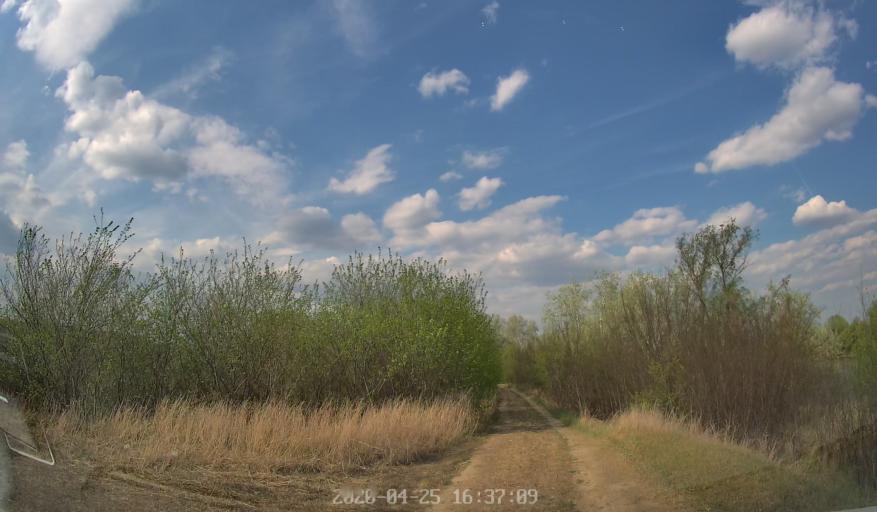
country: MD
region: Chisinau
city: Vadul lui Voda
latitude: 47.1122
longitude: 29.0653
